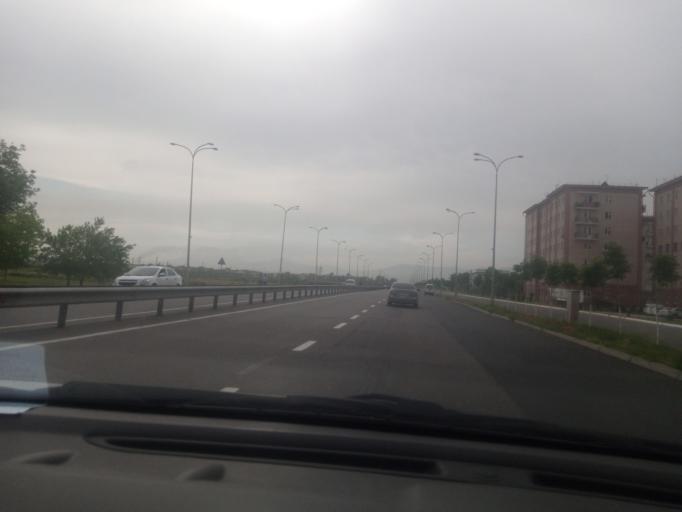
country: UZ
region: Toshkent
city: Ohangaron
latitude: 40.9140
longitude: 69.6100
